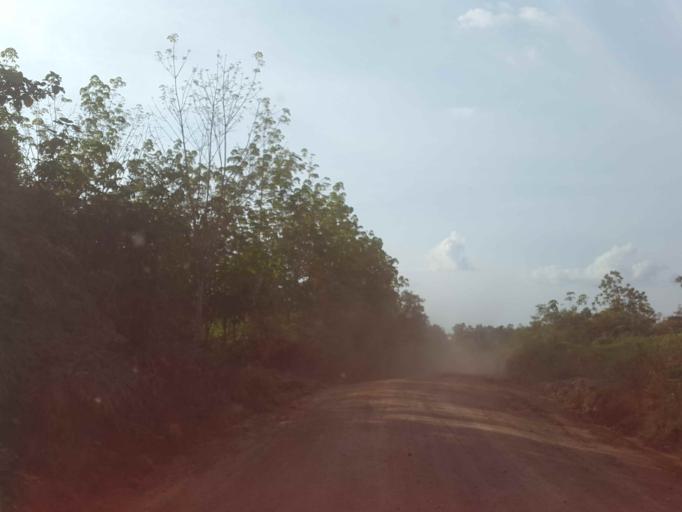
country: MY
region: Sarawak
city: Simanggang
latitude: 0.4873
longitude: 111.4273
